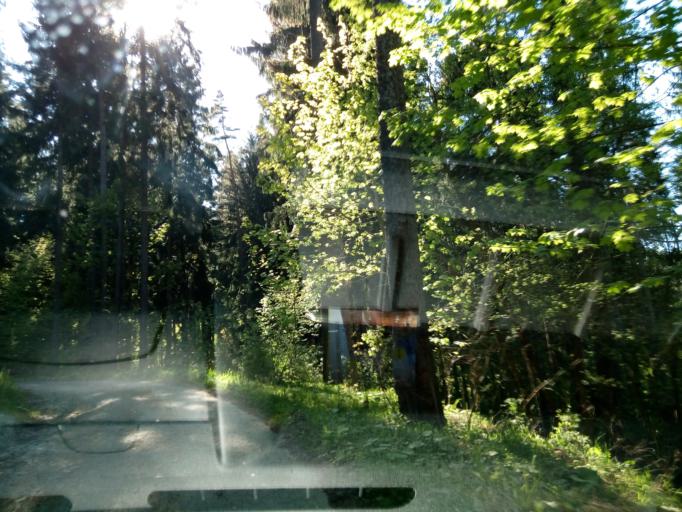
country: SK
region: Zilinsky
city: Ruzomberok
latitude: 49.0730
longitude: 19.2670
